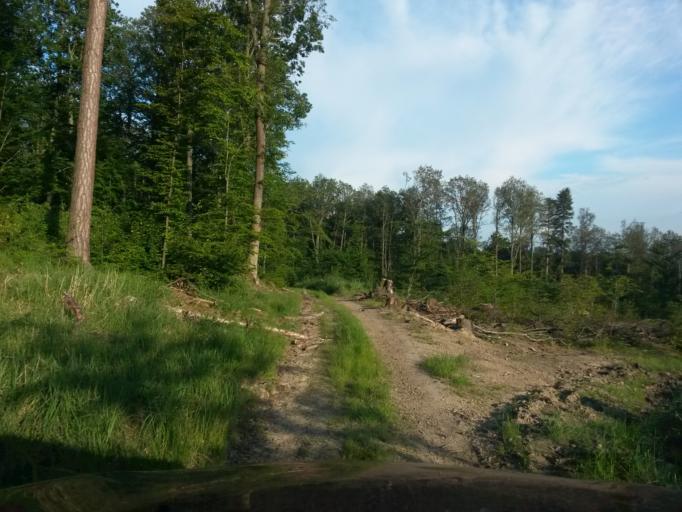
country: SK
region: Kosicky
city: Moldava nad Bodvou
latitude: 48.7344
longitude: 21.0418
